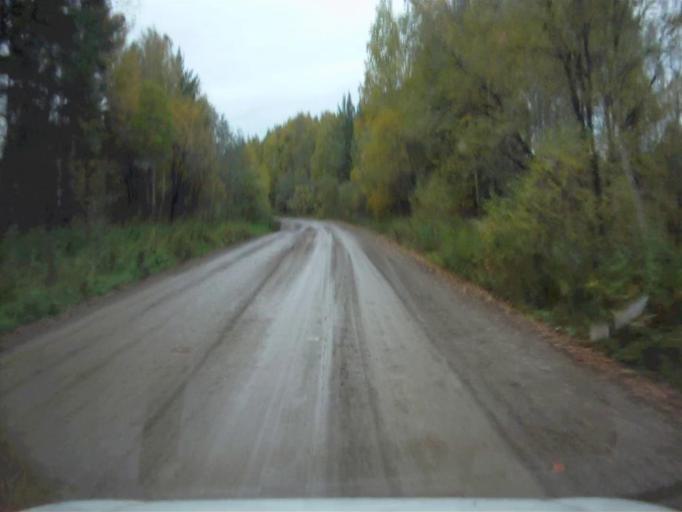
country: RU
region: Chelyabinsk
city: Nyazepetrovsk
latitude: 56.1040
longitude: 59.3857
